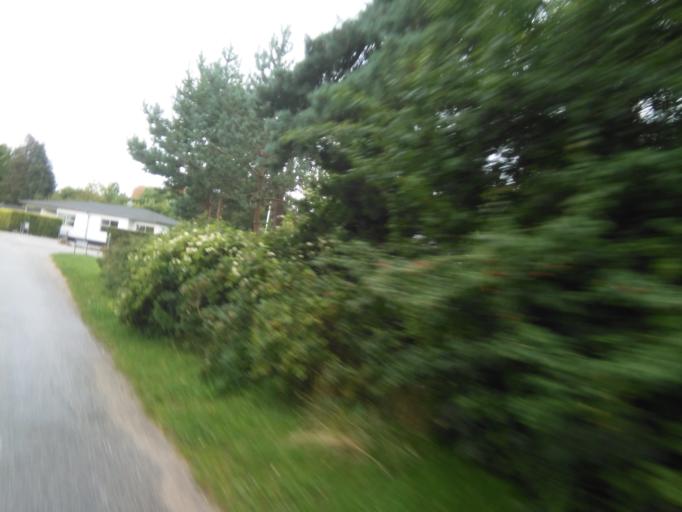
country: DK
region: Central Jutland
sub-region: Arhus Kommune
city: Logten
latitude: 56.2370
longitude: 10.3300
